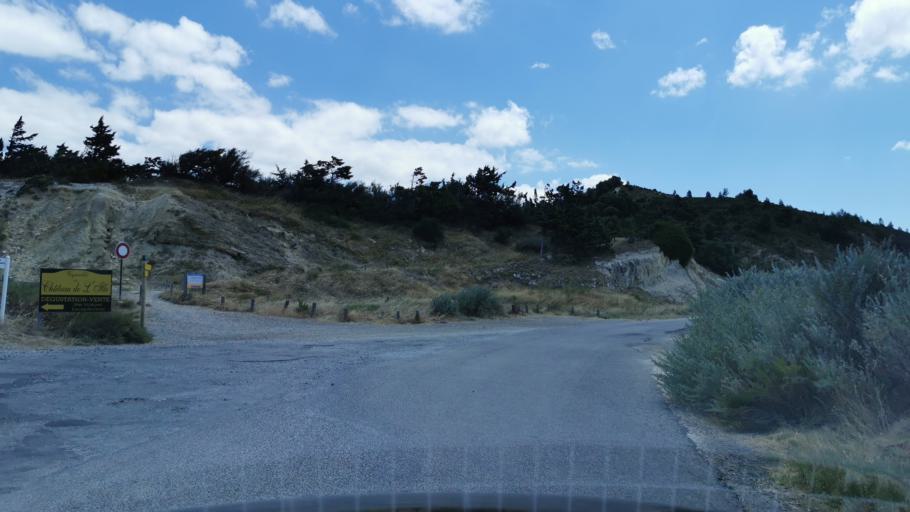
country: FR
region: Languedoc-Roussillon
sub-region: Departement de l'Aude
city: Peyriac-de-Mer
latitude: 43.0859
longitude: 2.9675
